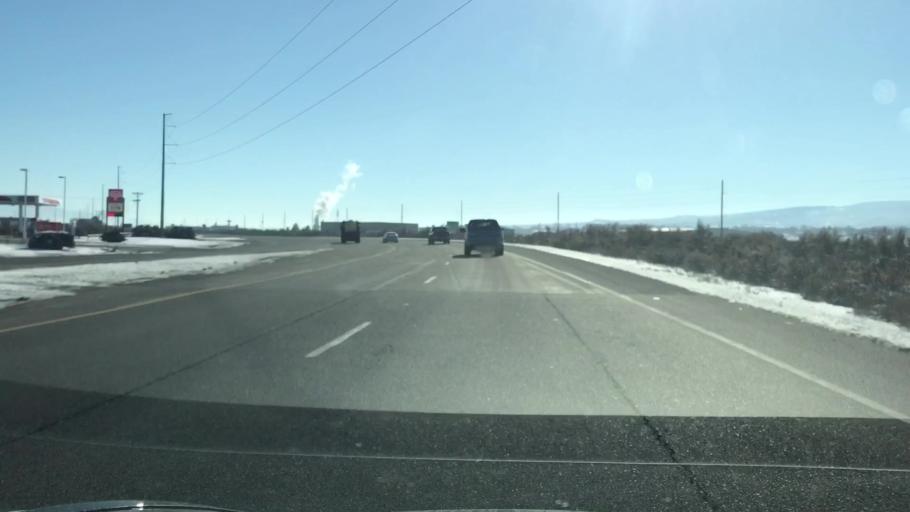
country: US
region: Colorado
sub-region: Mesa County
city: Redlands
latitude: 39.1093
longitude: -108.6423
